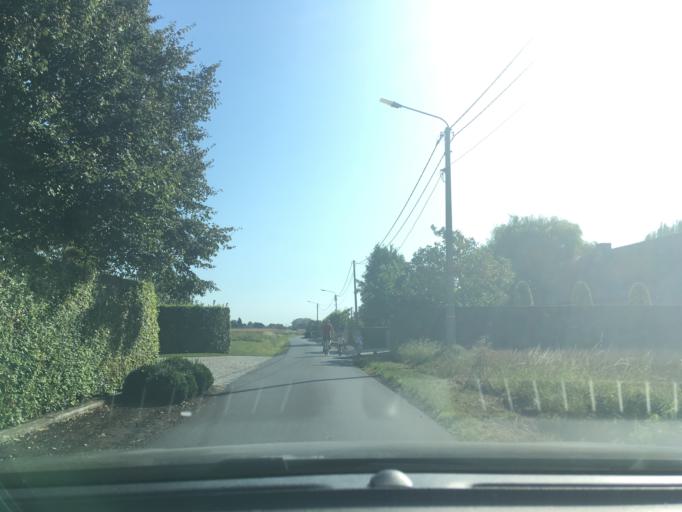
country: BE
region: Flanders
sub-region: Provincie West-Vlaanderen
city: Ledegem
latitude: 50.8770
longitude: 3.1409
